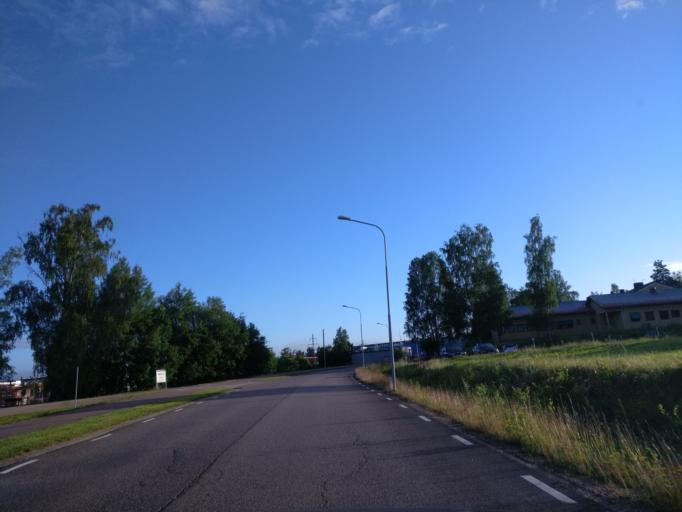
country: SE
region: Vaermland
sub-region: Hagfors Kommun
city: Hagfors
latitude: 60.0262
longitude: 13.6926
